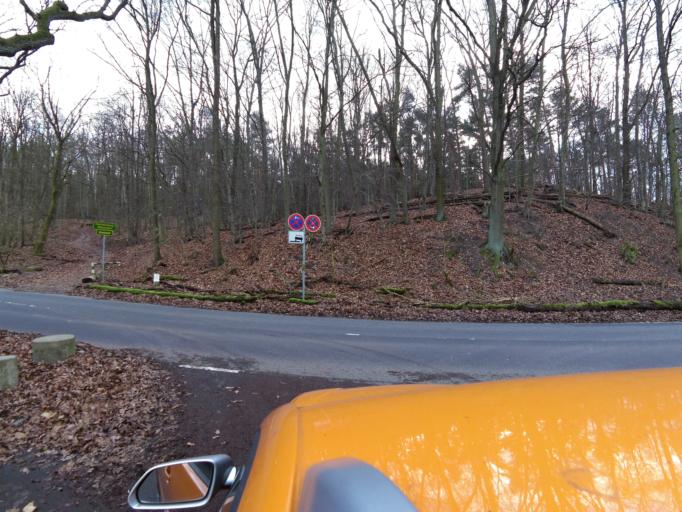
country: DE
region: Berlin
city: Gatow
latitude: 52.4691
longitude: 13.1977
